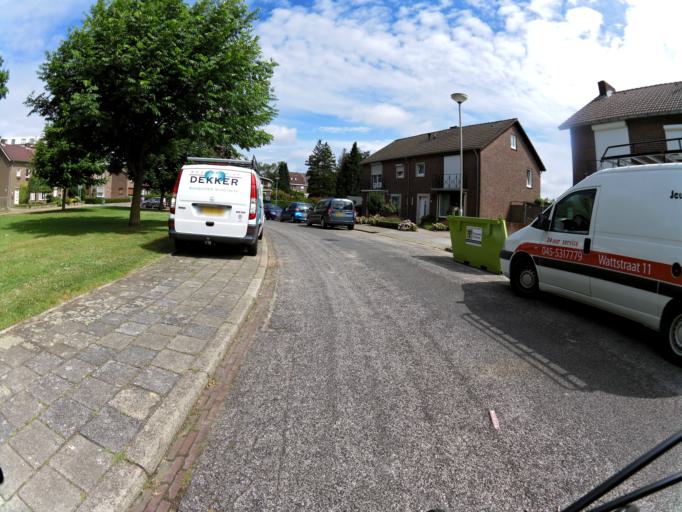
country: NL
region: Limburg
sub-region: Gemeente Heerlen
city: Heerlen
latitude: 50.8984
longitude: 6.0181
